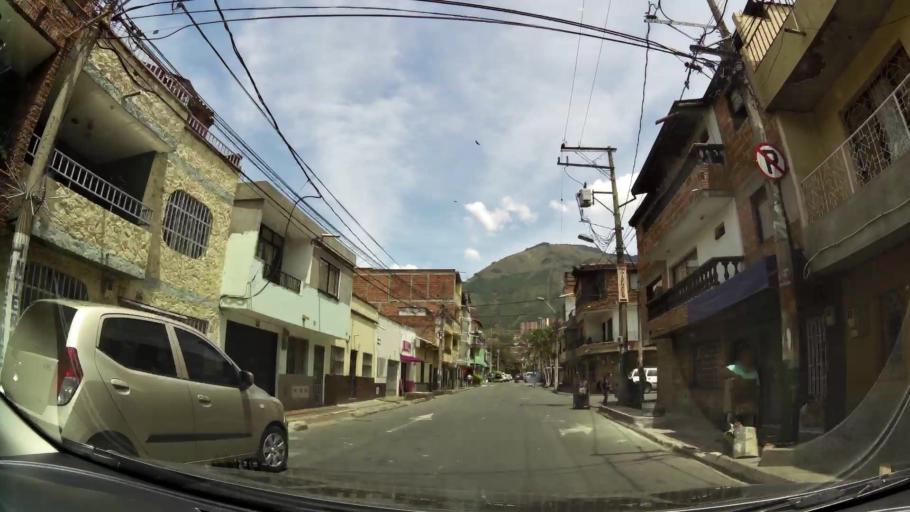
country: CO
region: Antioquia
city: Bello
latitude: 6.3382
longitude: -75.5555
